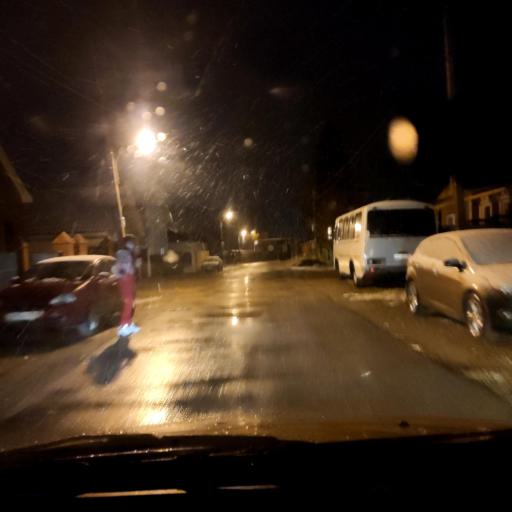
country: RU
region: Bashkortostan
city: Ufa
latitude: 54.7302
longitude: 55.9005
